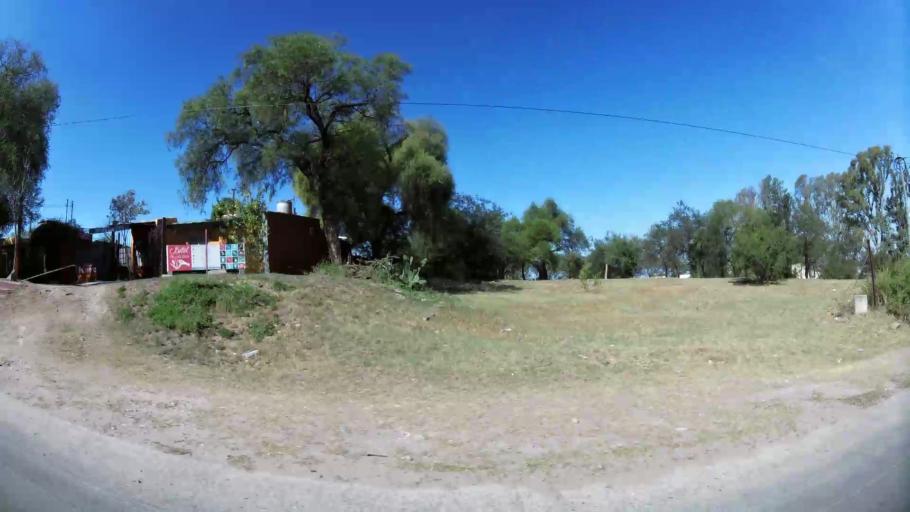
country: AR
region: Cordoba
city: Saldan
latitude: -31.3202
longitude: -64.2884
